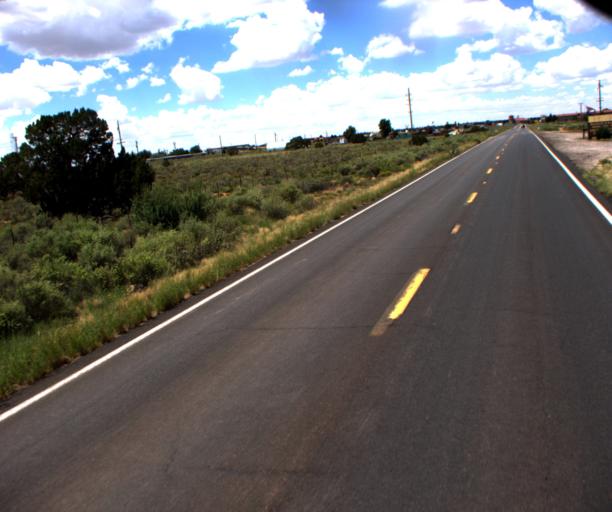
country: US
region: Arizona
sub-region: Coconino County
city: Grand Canyon Village
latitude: 35.6475
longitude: -112.1335
